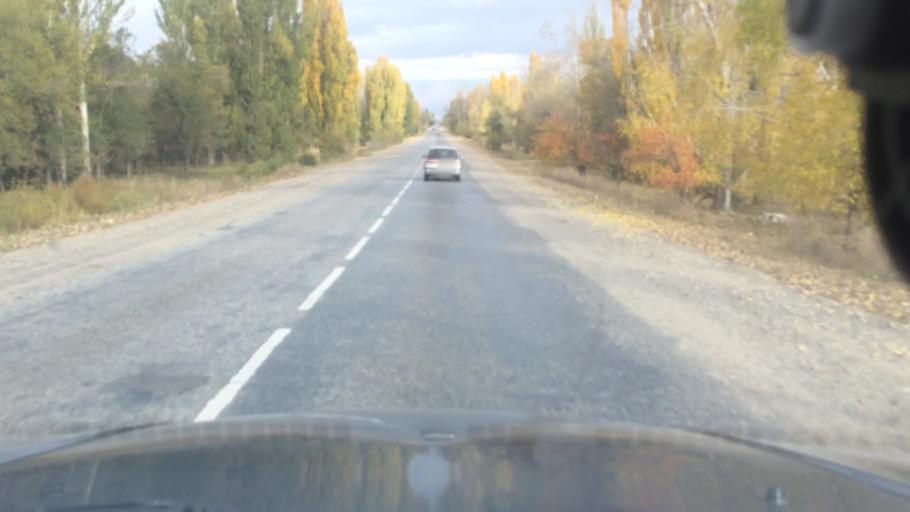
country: KG
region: Ysyk-Koel
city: Tyup
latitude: 42.6119
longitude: 78.3667
